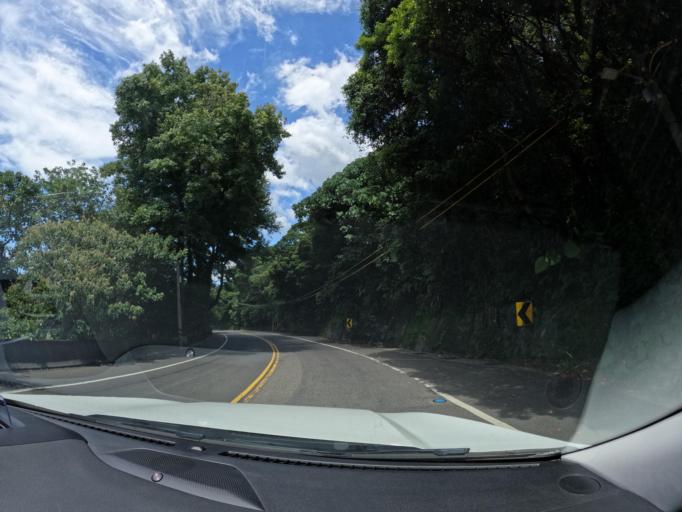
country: TW
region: Taipei
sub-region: Taipei
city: Banqiao
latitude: 25.1211
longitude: 121.3885
